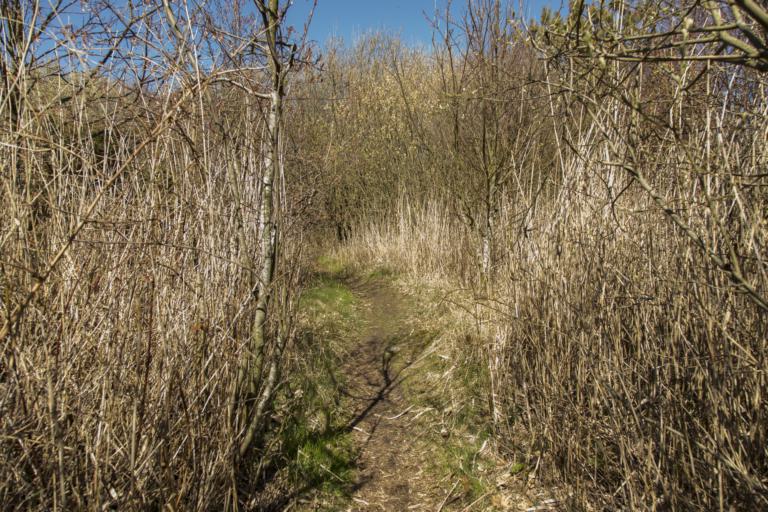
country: SE
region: Halland
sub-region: Varbergs Kommun
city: Traslovslage
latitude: 57.0464
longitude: 12.2866
